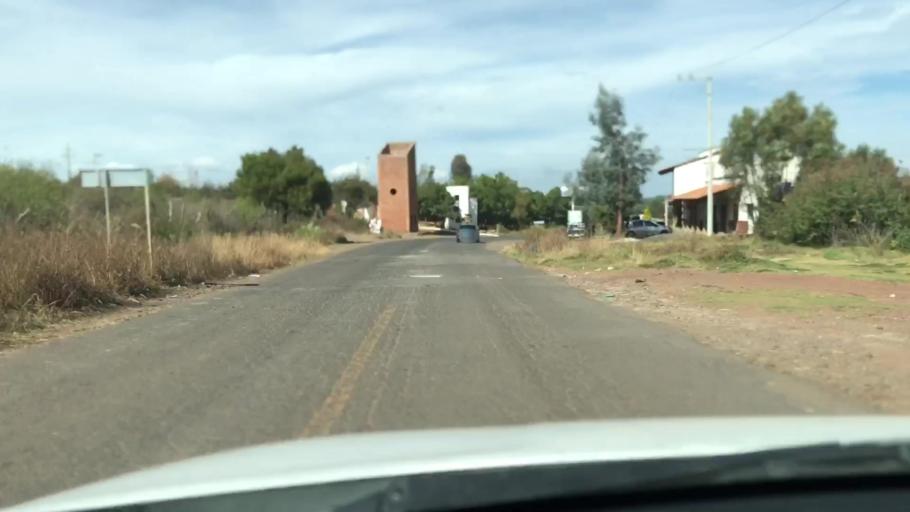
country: MX
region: Jalisco
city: Chiquilistlan
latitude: 20.1380
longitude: -103.7173
